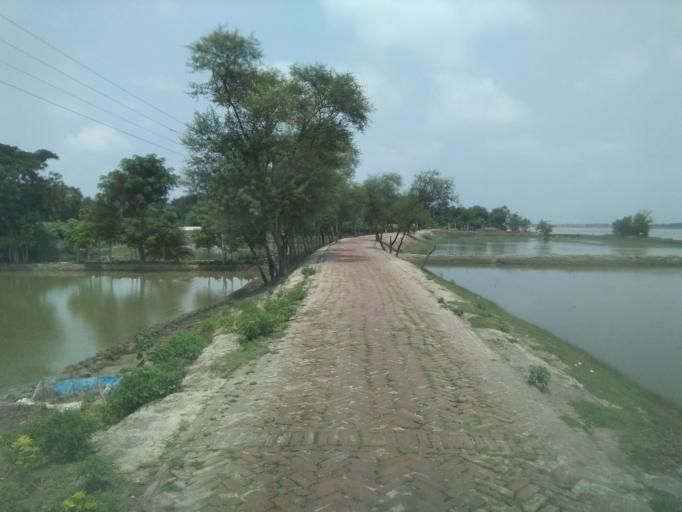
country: BD
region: Khulna
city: Phultala
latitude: 22.6412
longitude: 89.4254
